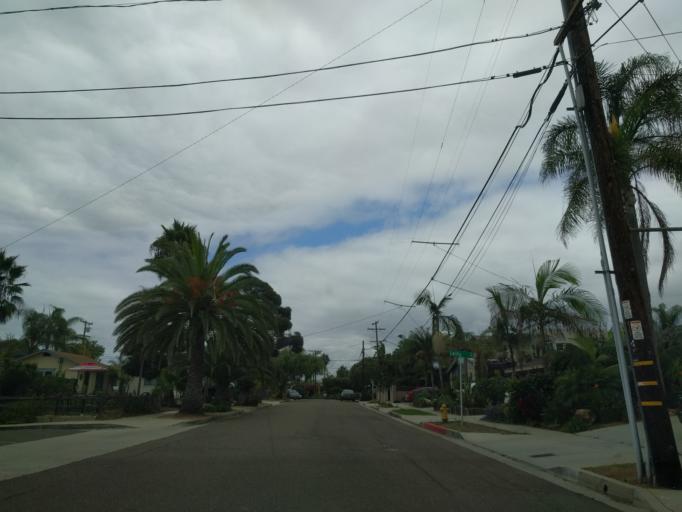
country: US
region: California
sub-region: San Diego County
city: Encinitas
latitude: 33.0514
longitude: -117.2974
